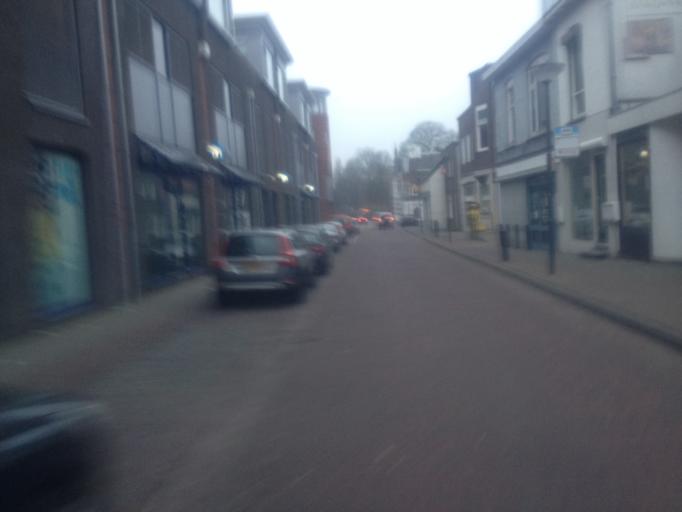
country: NL
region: Gelderland
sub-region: Gemeente Renkum
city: Renkum
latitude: 51.9718
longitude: 5.7282
